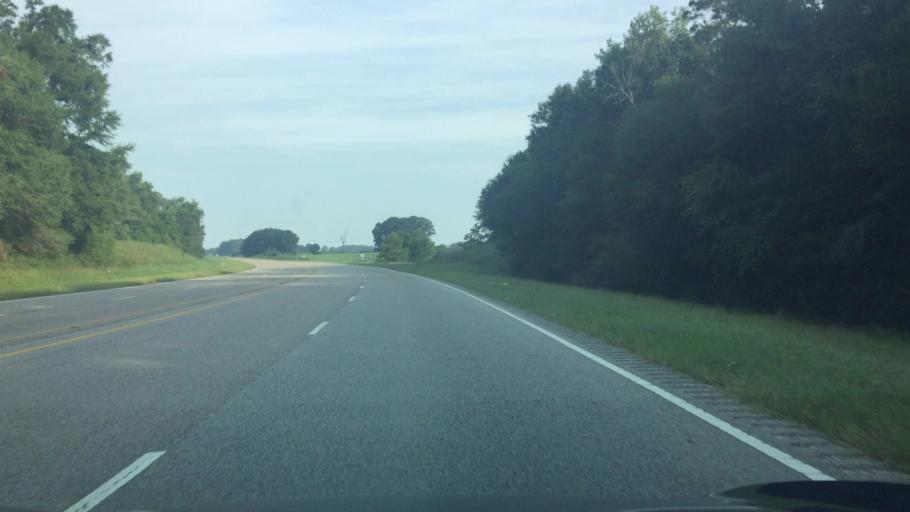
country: US
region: Alabama
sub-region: Covington County
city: Andalusia
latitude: 31.3976
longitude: -86.5770
